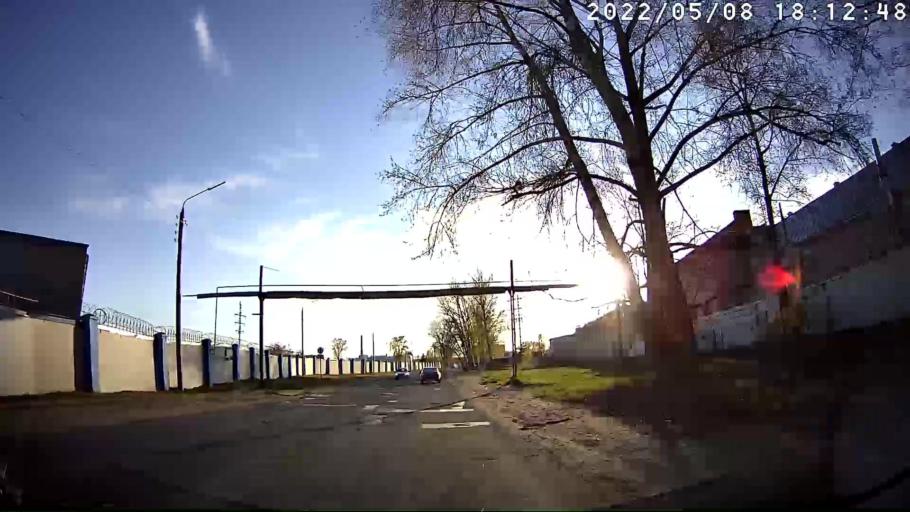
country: RU
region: Tatarstan
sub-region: Zelenodol'skiy Rayon
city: Zelenodolsk
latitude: 55.8407
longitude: 48.5020
